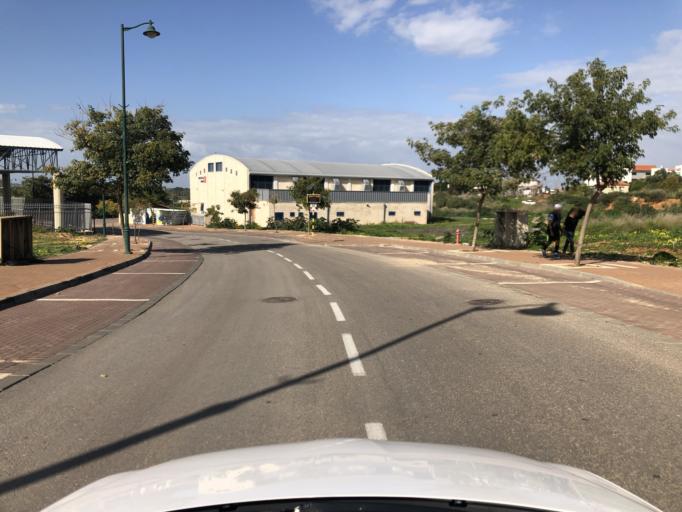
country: IL
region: Central District
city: Ness Ziona
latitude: 31.9094
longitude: 34.7862
